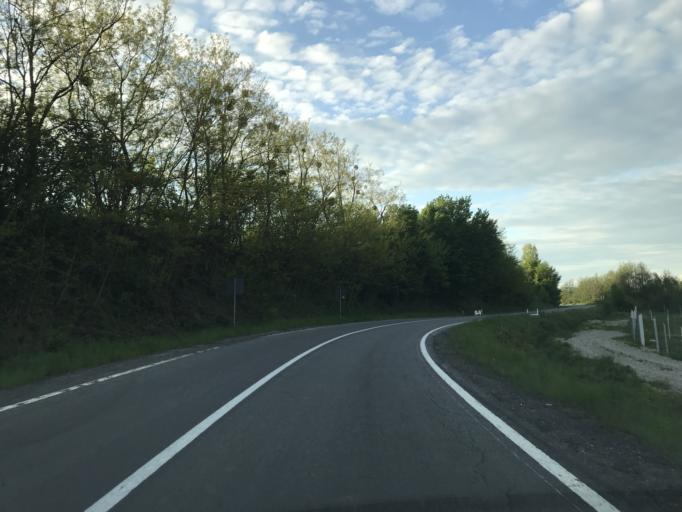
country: RO
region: Sibiu
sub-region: Comuna Cartisoara
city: Cartisoara
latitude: 45.6999
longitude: 24.5703
